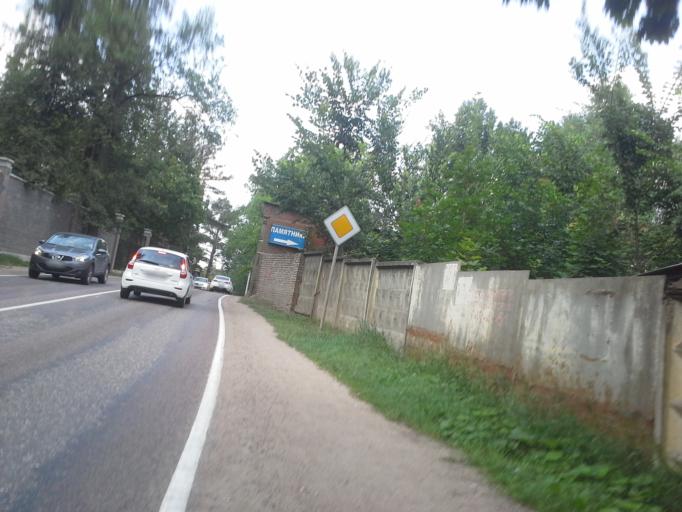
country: RU
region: Moskovskaya
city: Istra
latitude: 55.8954
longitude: 36.7939
